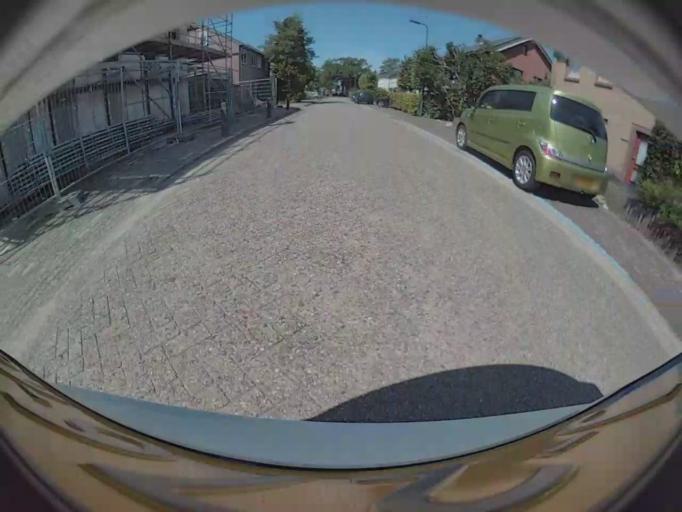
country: NL
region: North Brabant
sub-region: Gemeente 's-Hertogenbosch
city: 's-Hertogenbosch
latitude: 51.7174
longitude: 5.3610
